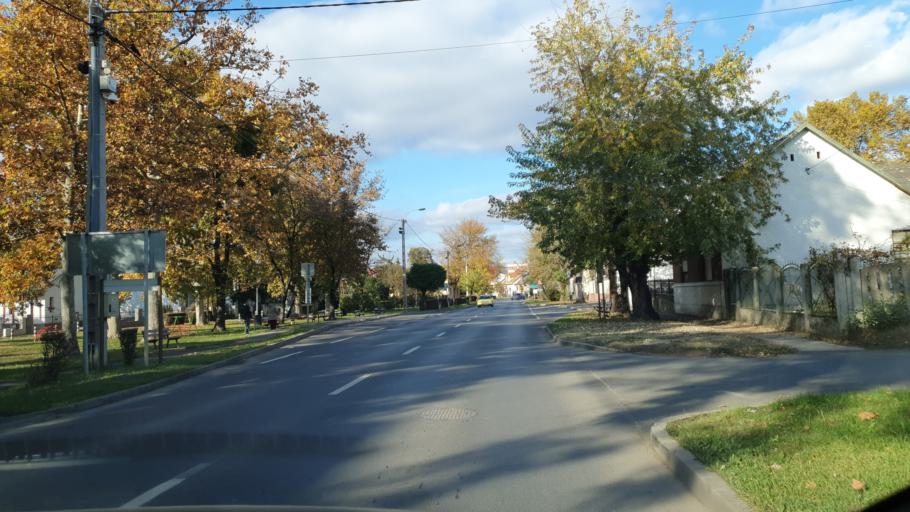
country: HU
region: Szabolcs-Szatmar-Bereg
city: Kisvarda
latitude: 48.2169
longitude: 22.0829
